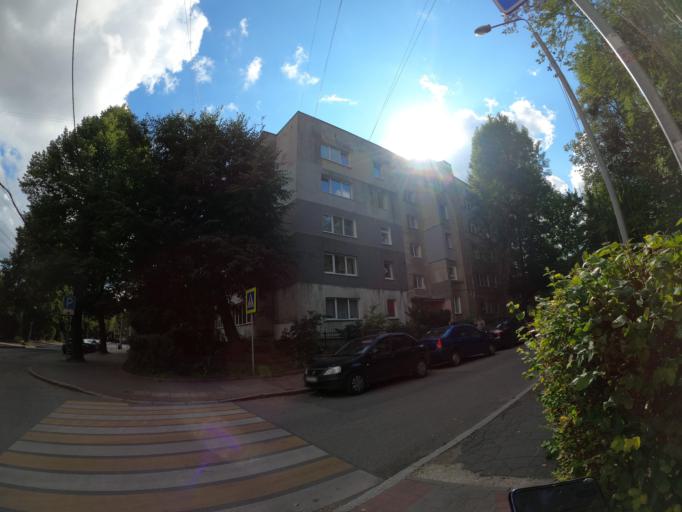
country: RU
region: Kaliningrad
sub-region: Gorod Kaliningrad
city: Kaliningrad
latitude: 54.7308
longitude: 20.4783
